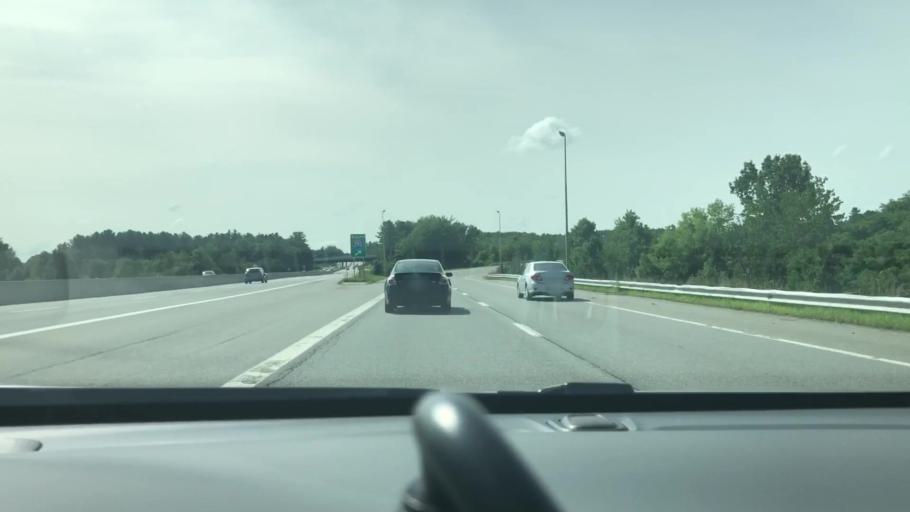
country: US
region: New Hampshire
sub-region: Hillsborough County
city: Bedford
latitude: 42.9552
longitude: -71.4744
